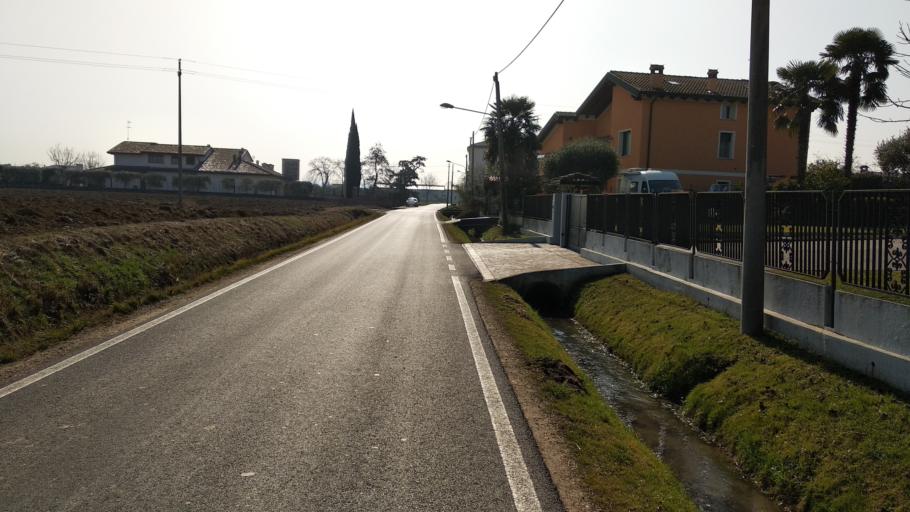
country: IT
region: Veneto
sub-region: Provincia di Vicenza
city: Crispi Cavour
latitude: 45.5857
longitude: 11.5173
